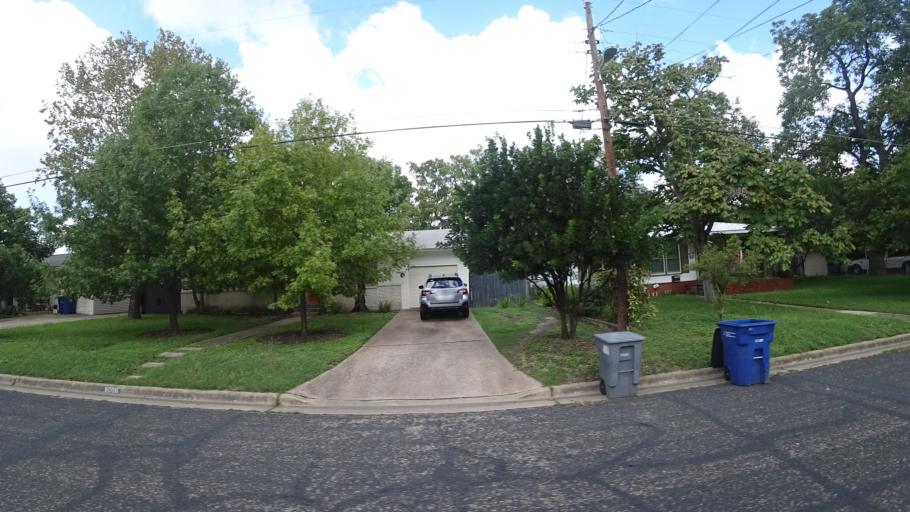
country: US
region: Texas
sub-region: Travis County
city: Austin
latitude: 30.3529
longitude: -97.7178
